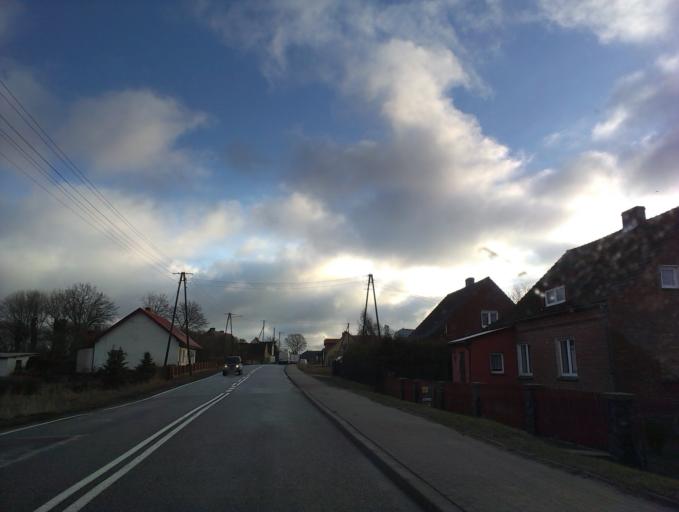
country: PL
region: West Pomeranian Voivodeship
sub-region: Powiat szczecinecki
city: Szczecinek
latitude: 53.7339
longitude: 16.8090
